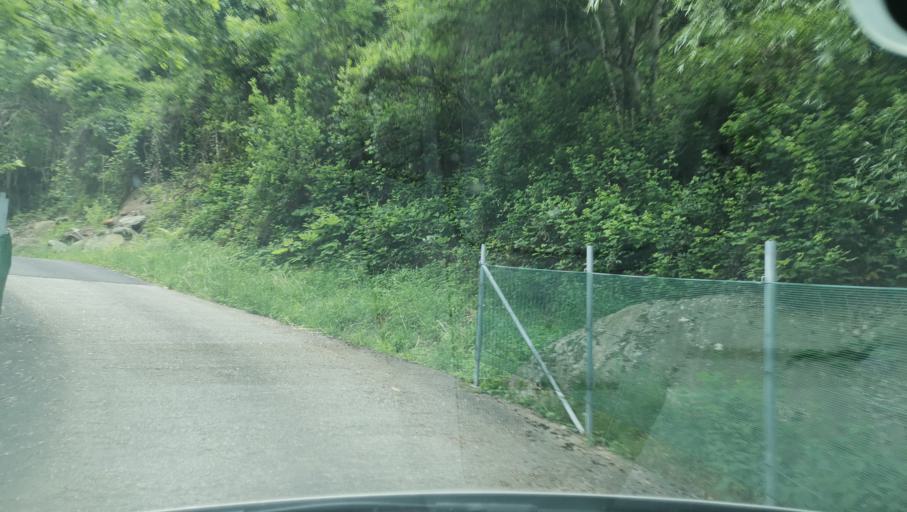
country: IT
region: Piedmont
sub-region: Provincia di Torino
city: Tavagnasco
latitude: 45.5335
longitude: 7.8166
